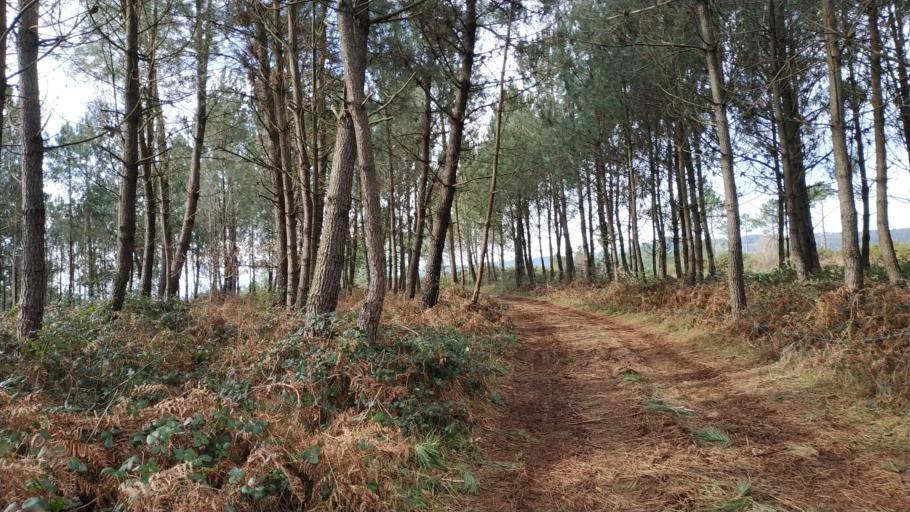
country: ES
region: Galicia
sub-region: Provincia de Pontevedra
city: Silleda
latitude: 42.7728
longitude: -8.1630
